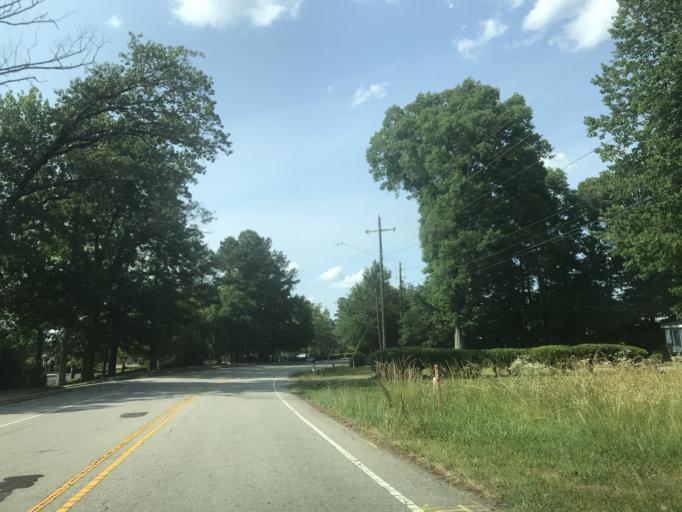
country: US
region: North Carolina
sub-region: Wake County
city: Cary
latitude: 35.7943
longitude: -78.7352
